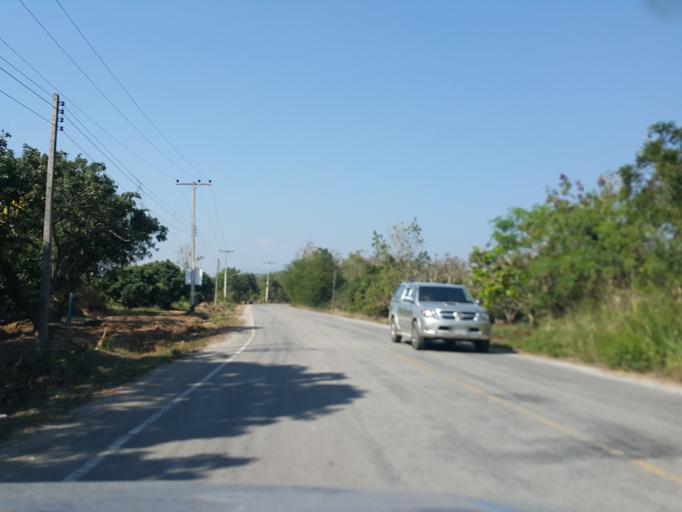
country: TH
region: Chiang Mai
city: Doi Lo
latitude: 18.5312
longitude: 98.7803
